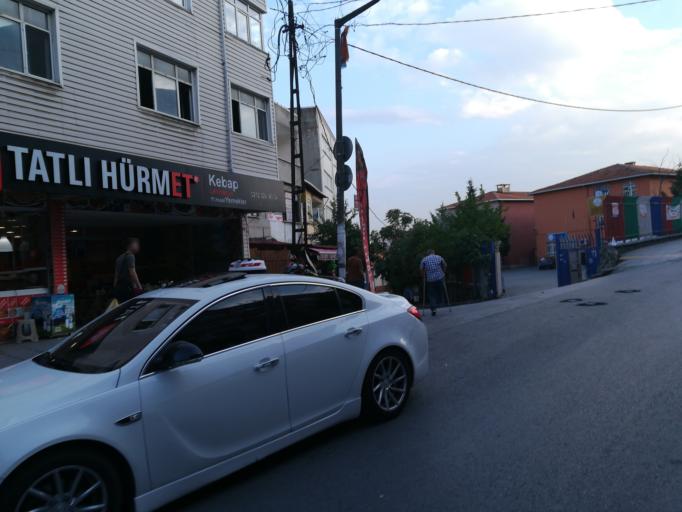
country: TR
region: Istanbul
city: Sisli
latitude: 41.0988
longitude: 28.9918
